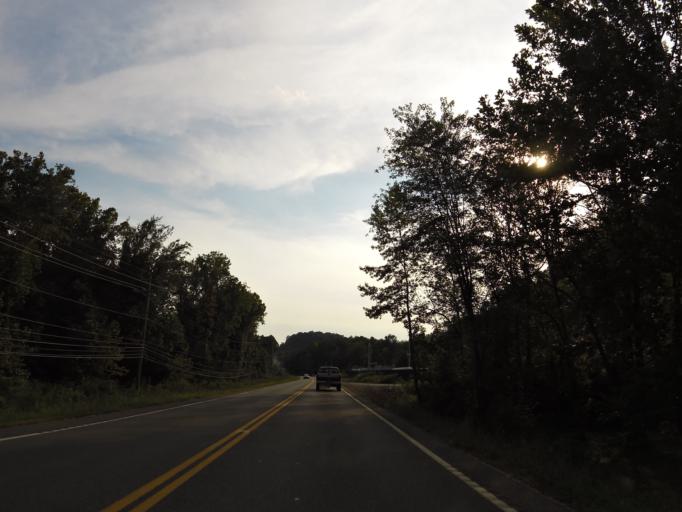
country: US
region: Tennessee
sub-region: Roane County
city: Oliver Springs
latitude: 36.0474
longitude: -84.3597
